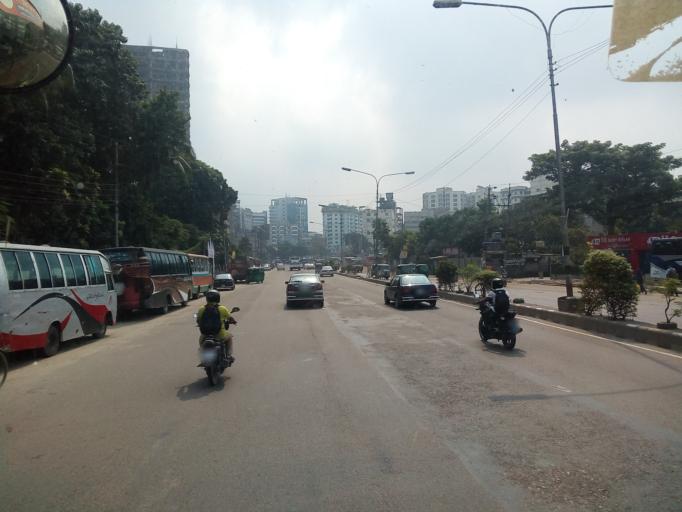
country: BD
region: Dhaka
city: Azimpur
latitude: 23.7792
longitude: 90.3572
